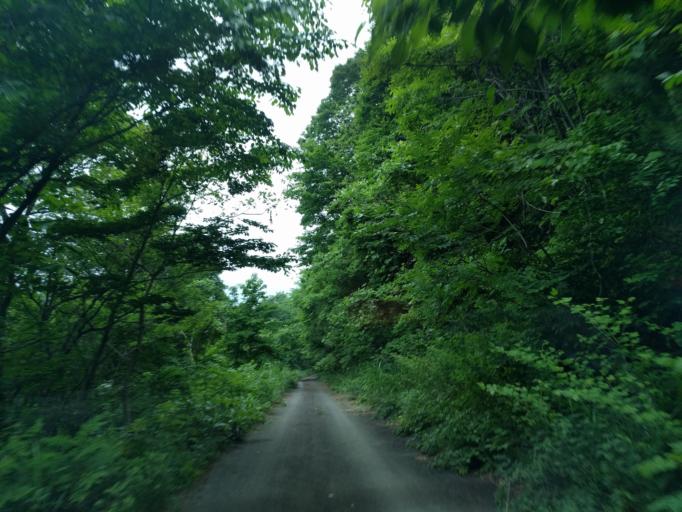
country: JP
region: Fukushima
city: Inawashiro
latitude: 37.4452
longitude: 140.0297
